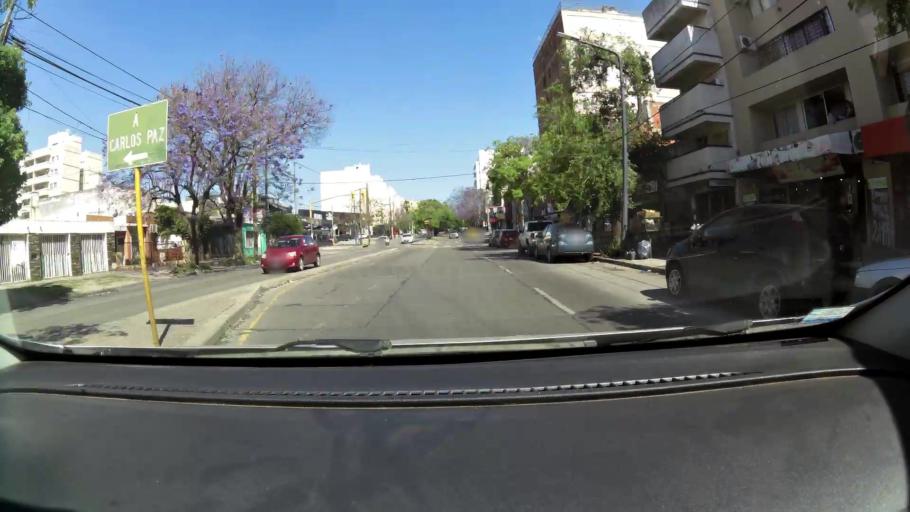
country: AR
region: Cordoba
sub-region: Departamento de Capital
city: Cordoba
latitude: -31.4118
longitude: -64.2087
